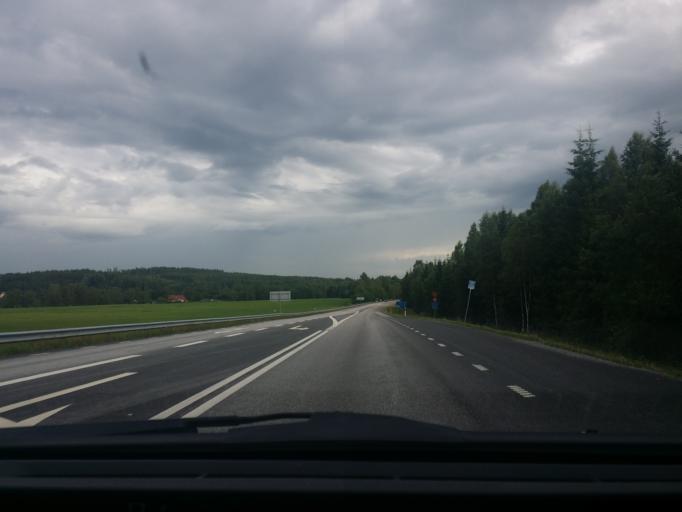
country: SE
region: OErebro
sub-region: Nora Kommun
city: Nora
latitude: 59.4932
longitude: 15.0520
